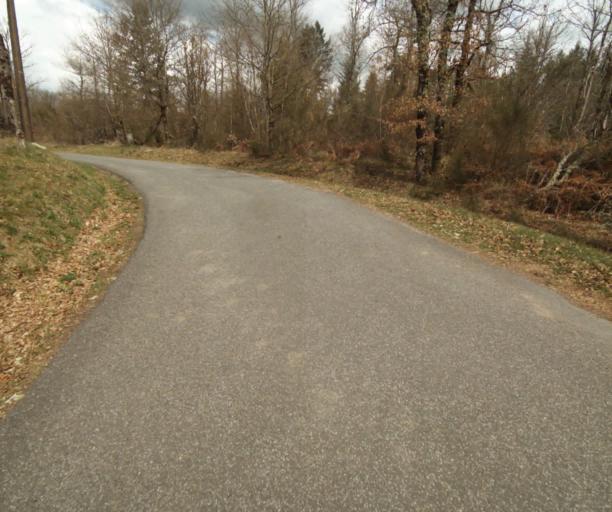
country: FR
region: Limousin
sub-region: Departement de la Correze
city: Correze
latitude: 45.3466
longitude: 1.9390
